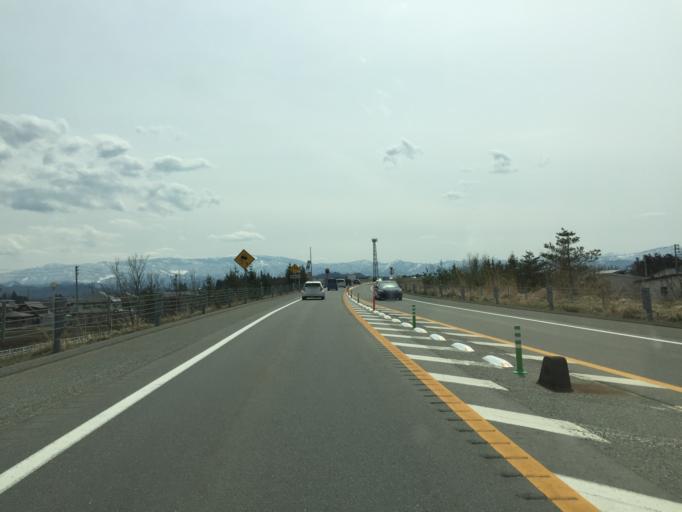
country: JP
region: Yamagata
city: Takahata
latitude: 37.9908
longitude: 140.1560
